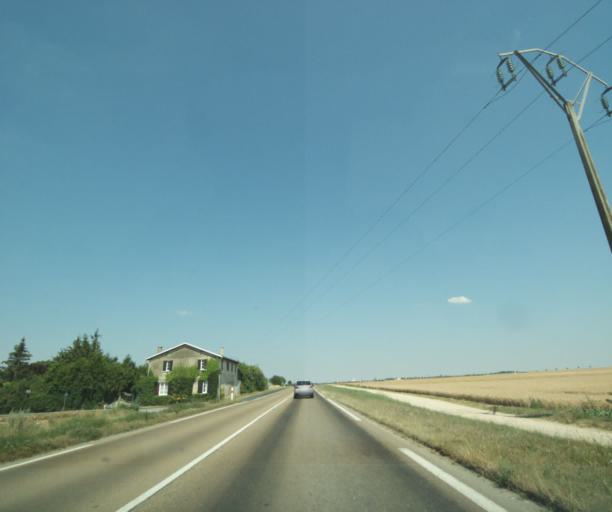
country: FR
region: Champagne-Ardenne
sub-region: Departement de la Marne
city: Sarry
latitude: 48.9224
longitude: 4.4166
